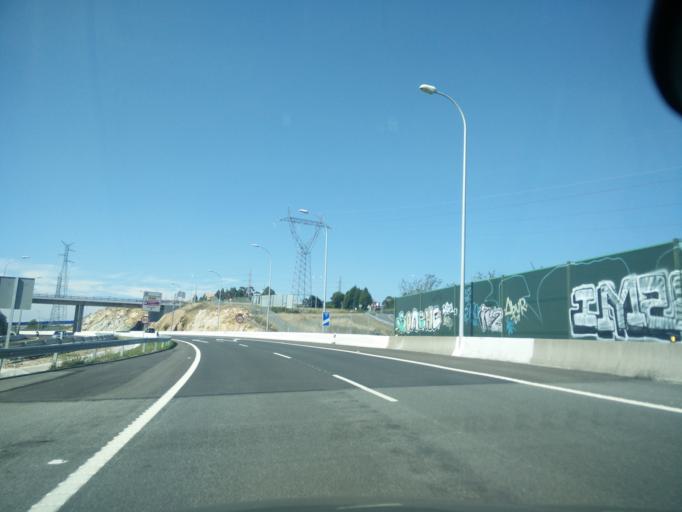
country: ES
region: Galicia
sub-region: Provincia da Coruna
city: Culleredo
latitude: 43.3212
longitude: -8.4088
